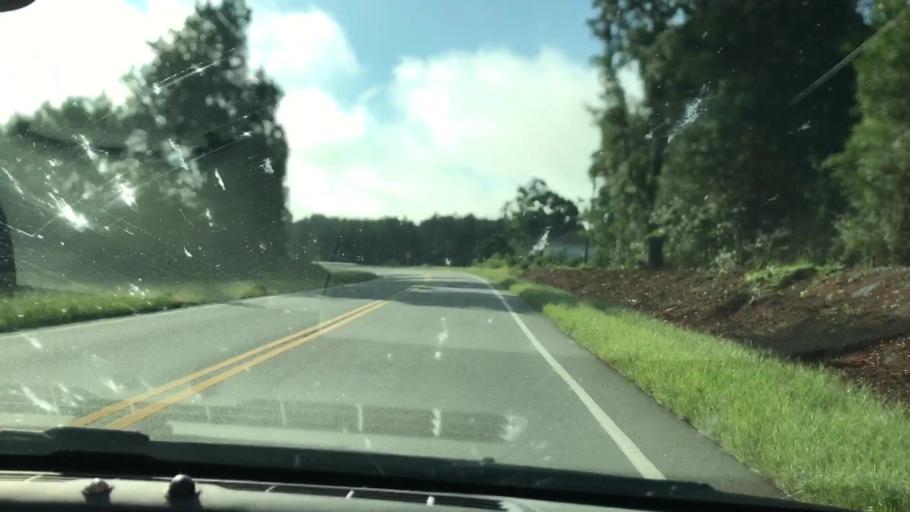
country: US
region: Georgia
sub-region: Terrell County
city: Dawson
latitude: 31.7708
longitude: -84.5028
